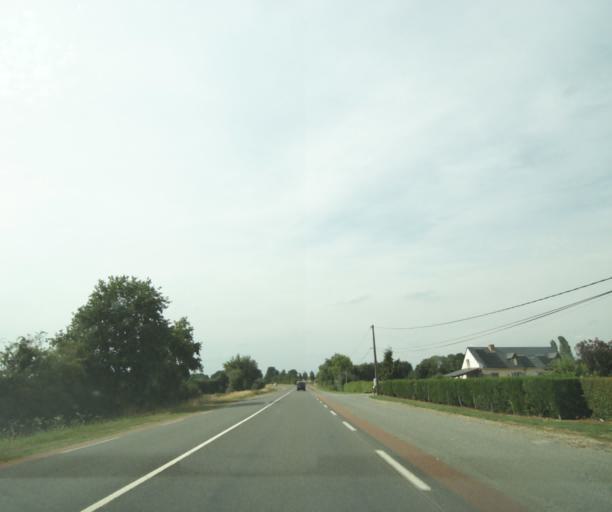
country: FR
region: Pays de la Loire
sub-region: Departement de la Sarthe
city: Luceau
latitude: 47.7375
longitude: 0.3913
